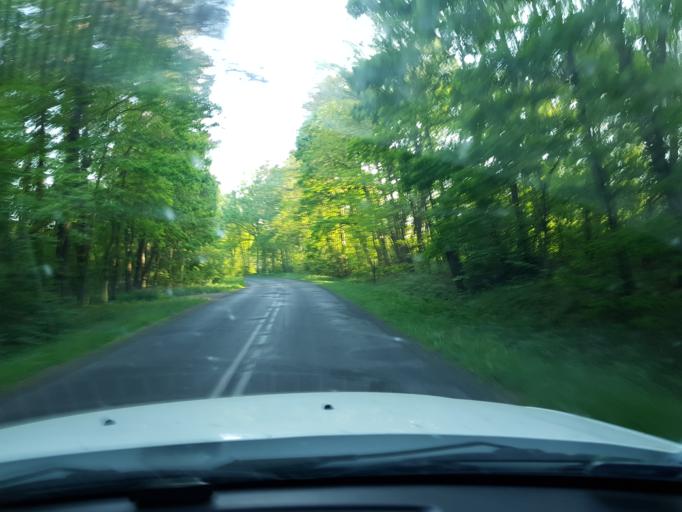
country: PL
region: West Pomeranian Voivodeship
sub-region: Powiat stargardzki
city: Kobylanka
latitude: 53.4396
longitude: 14.9107
